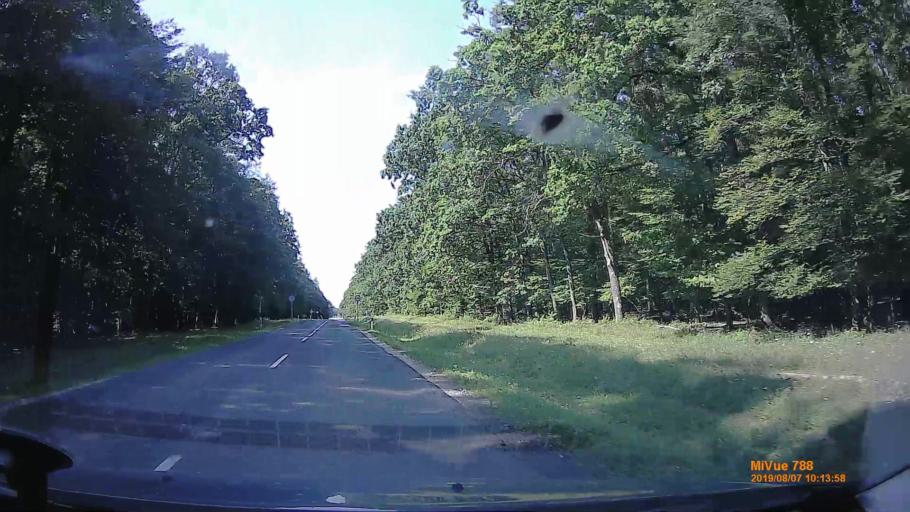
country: HU
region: Zala
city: Lenti
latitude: 46.6615
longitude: 16.6345
